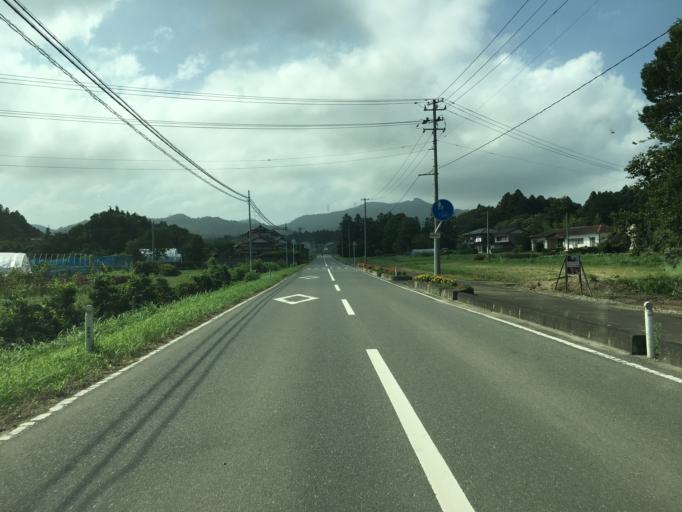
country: JP
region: Miyagi
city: Marumori
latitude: 37.8401
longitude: 140.8973
